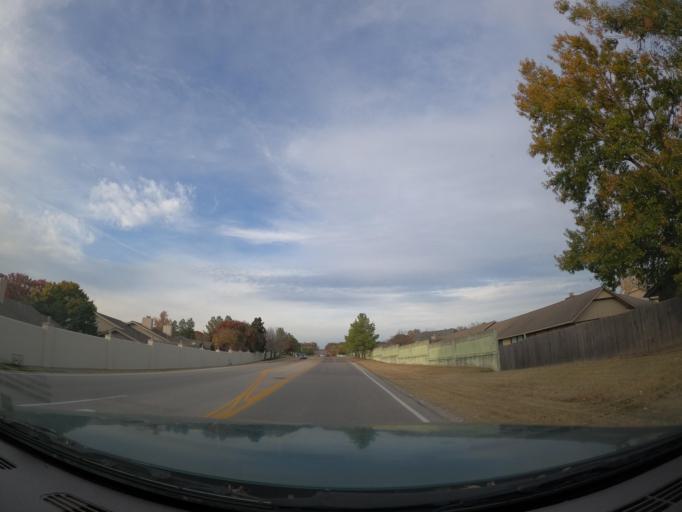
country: US
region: Oklahoma
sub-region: Tulsa County
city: Jenks
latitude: 36.0589
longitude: -95.9400
